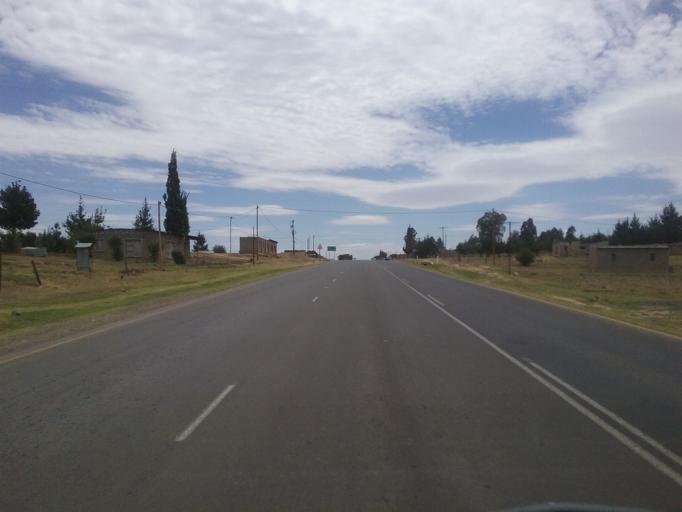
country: LS
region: Maseru
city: Maseru
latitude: -29.4921
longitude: 27.5276
